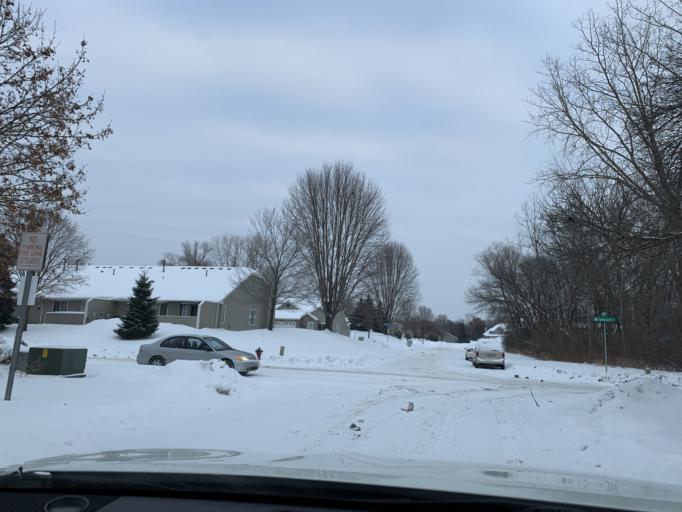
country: US
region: Minnesota
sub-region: Anoka County
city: Coon Rapids
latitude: 45.1643
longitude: -93.2923
